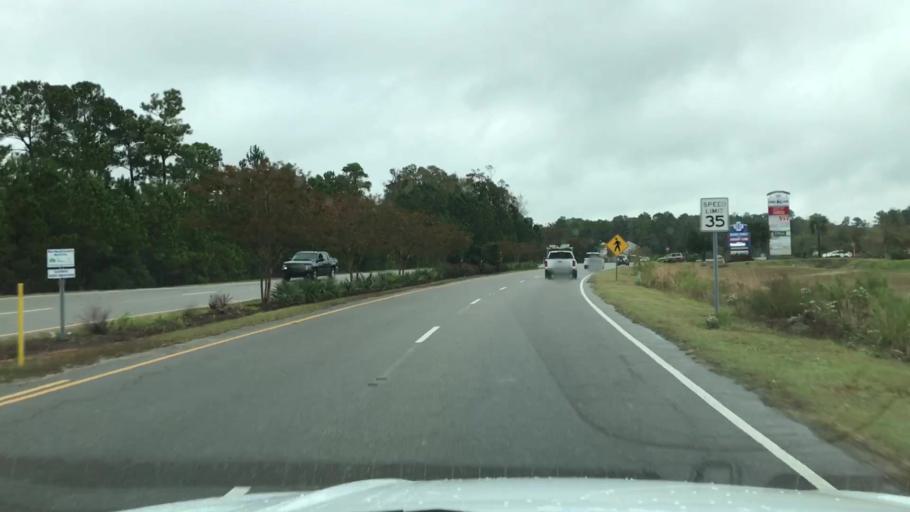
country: US
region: South Carolina
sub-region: Horry County
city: Myrtle Beach
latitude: 33.7541
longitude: -78.8673
